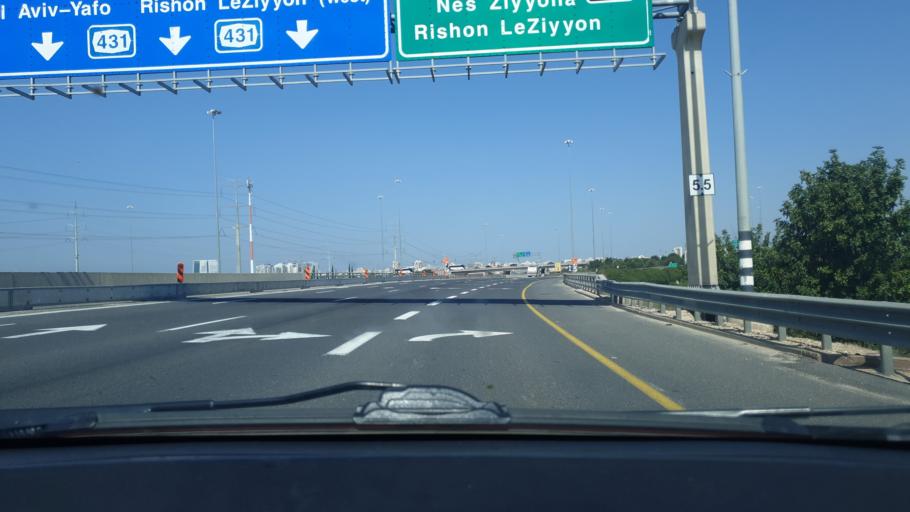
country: IL
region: Central District
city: Ness Ziona
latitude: 31.9358
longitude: 34.8175
